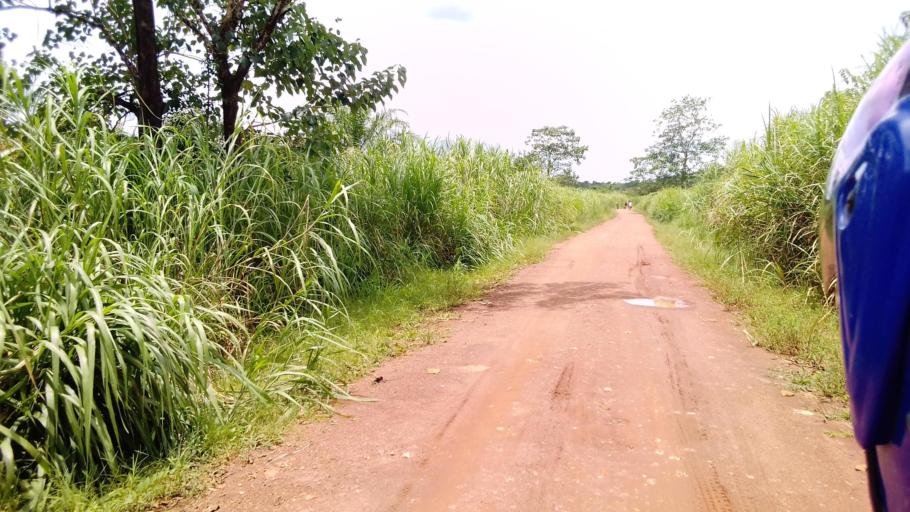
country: SL
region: Eastern Province
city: Koidu
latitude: 8.6750
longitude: -10.9357
